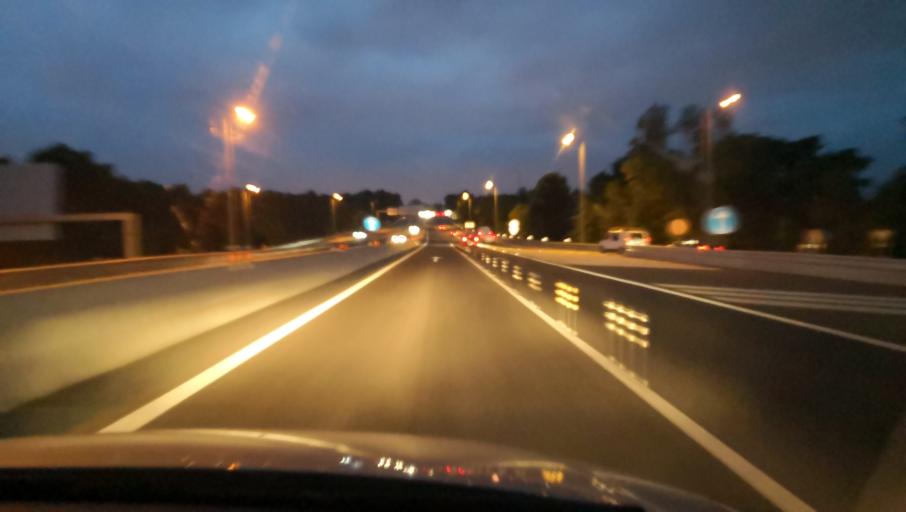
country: PT
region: Setubal
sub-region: Barreiro
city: Santo Antonio da Charneca
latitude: 38.6060
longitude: -9.0215
